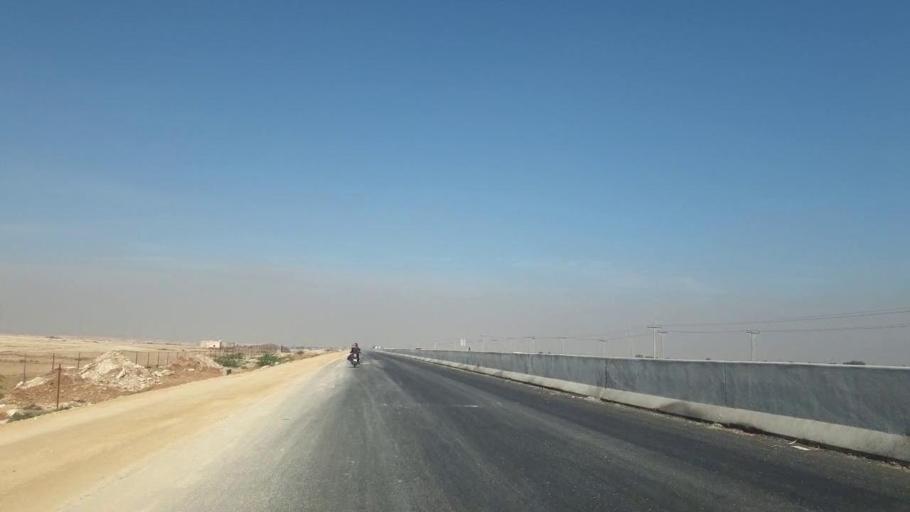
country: PK
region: Sindh
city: Jamshoro
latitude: 25.5034
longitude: 68.2729
